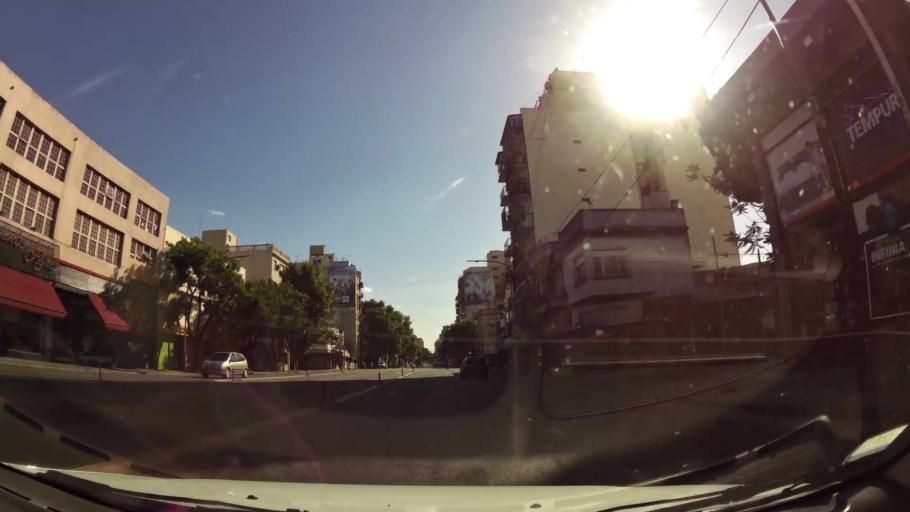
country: AR
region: Buenos Aires F.D.
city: Villa Santa Rita
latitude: -34.6121
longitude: -58.4695
